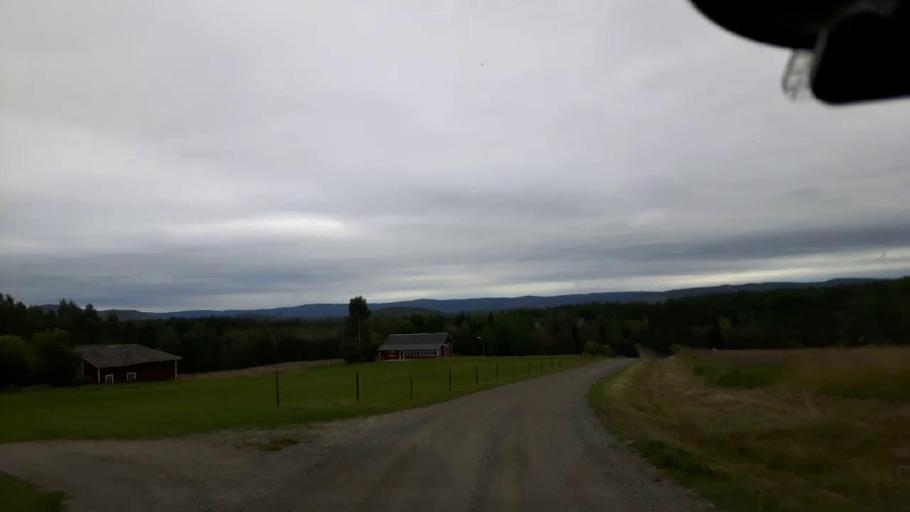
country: SE
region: Vaesternorrland
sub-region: Ange Kommun
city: Fransta
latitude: 62.8674
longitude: 15.9851
